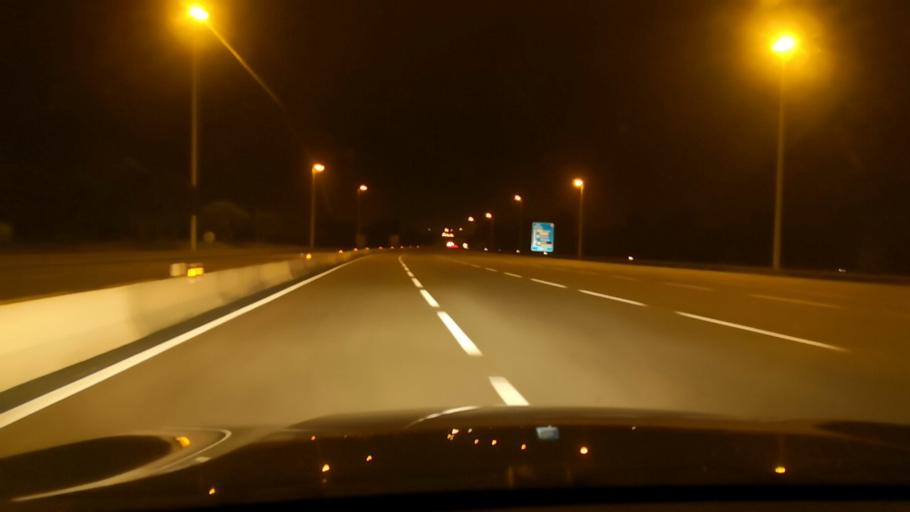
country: PT
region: Setubal
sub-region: Palmela
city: Palmela
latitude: 38.5676
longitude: -8.8665
